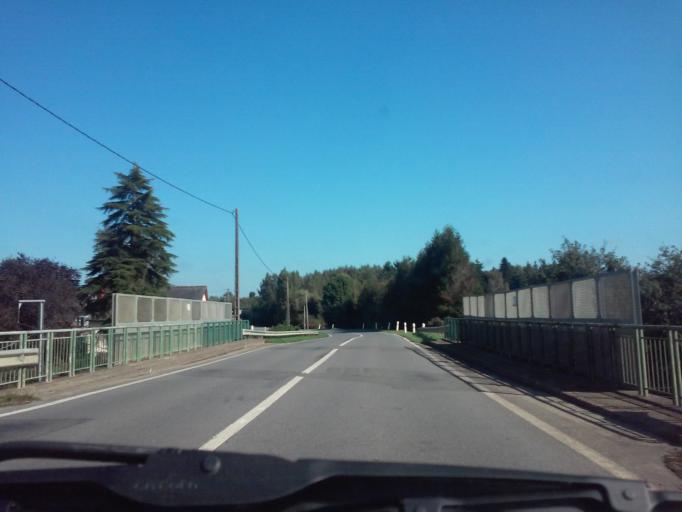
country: FR
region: Brittany
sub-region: Departement d'Ille-et-Vilaine
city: Chevaigne
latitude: 48.2054
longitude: -1.6267
